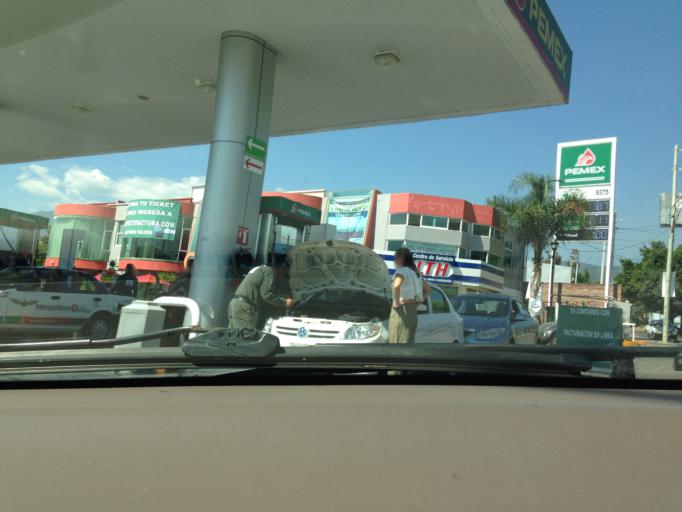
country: MX
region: Morelos
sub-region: Cuernavaca
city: Fraccionamiento Lomas de Ahuatlan
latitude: 18.9571
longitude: -99.2374
